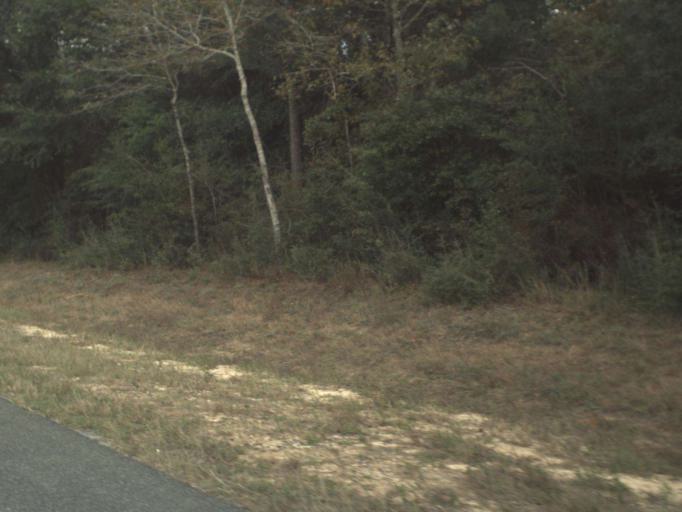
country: US
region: Florida
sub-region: Santa Rosa County
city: Point Baker
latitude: 30.7269
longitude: -87.0822
